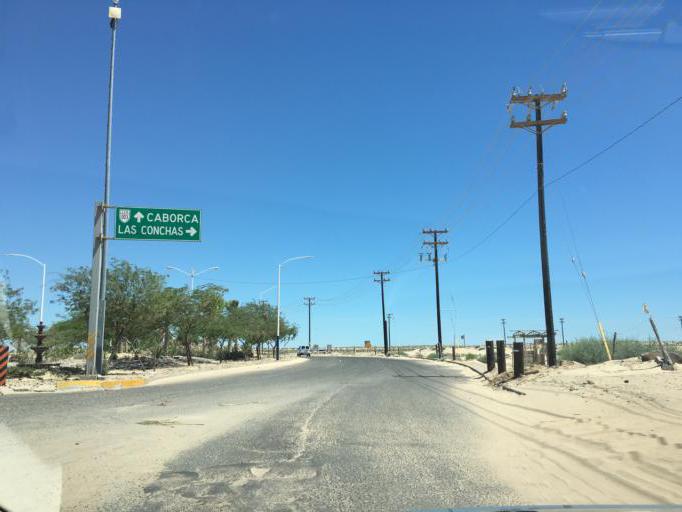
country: MX
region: Sonora
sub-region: Puerto Penasco
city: Puerto Penasco
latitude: 31.3058
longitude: -113.5202
